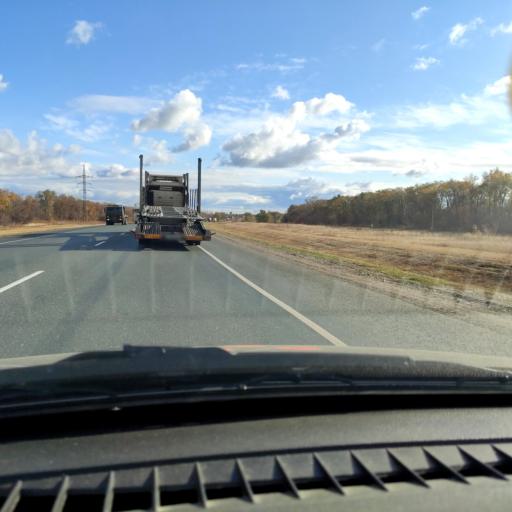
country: RU
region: Samara
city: Varlamovo
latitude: 53.1965
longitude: 48.3076
